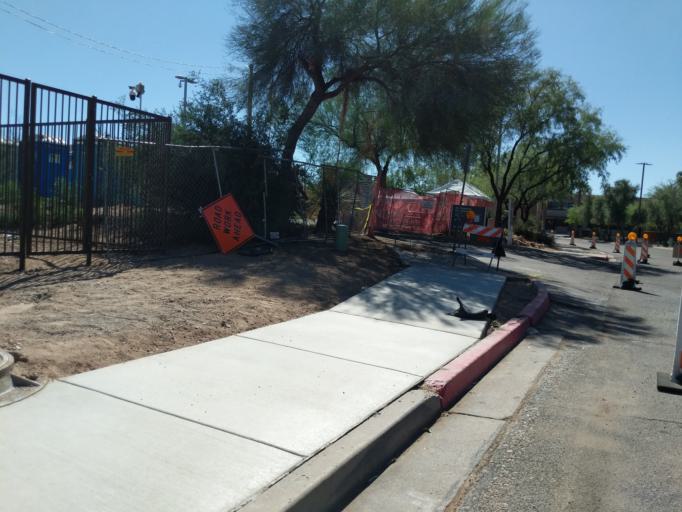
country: US
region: Arizona
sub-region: Pima County
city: Tucson
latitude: 32.2173
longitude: -110.8803
